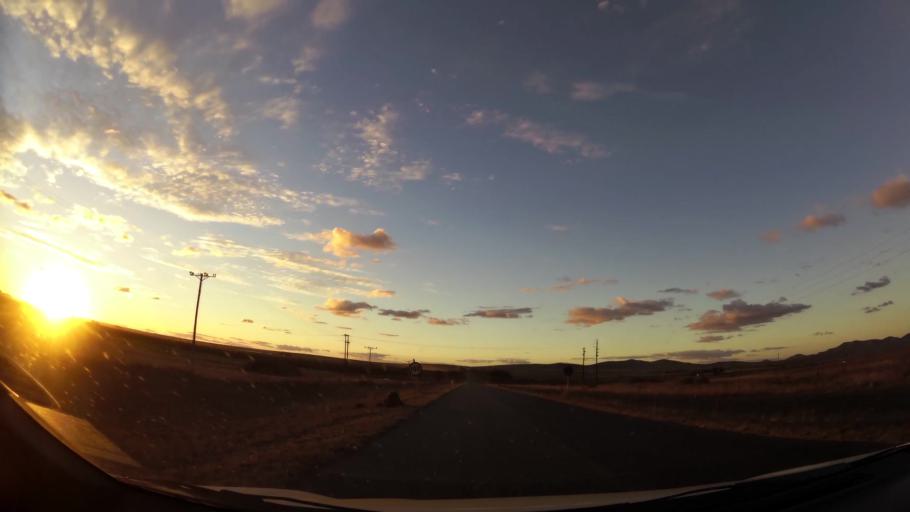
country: ZA
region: Limpopo
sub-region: Capricorn District Municipality
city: Polokwane
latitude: -23.7566
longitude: 29.4731
